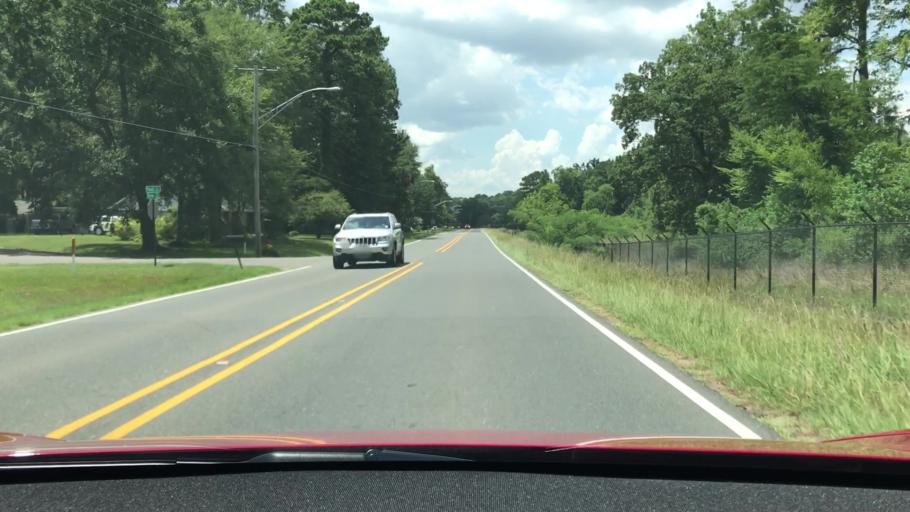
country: US
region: Louisiana
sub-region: Bossier Parish
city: Bossier City
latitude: 32.3872
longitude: -93.7183
